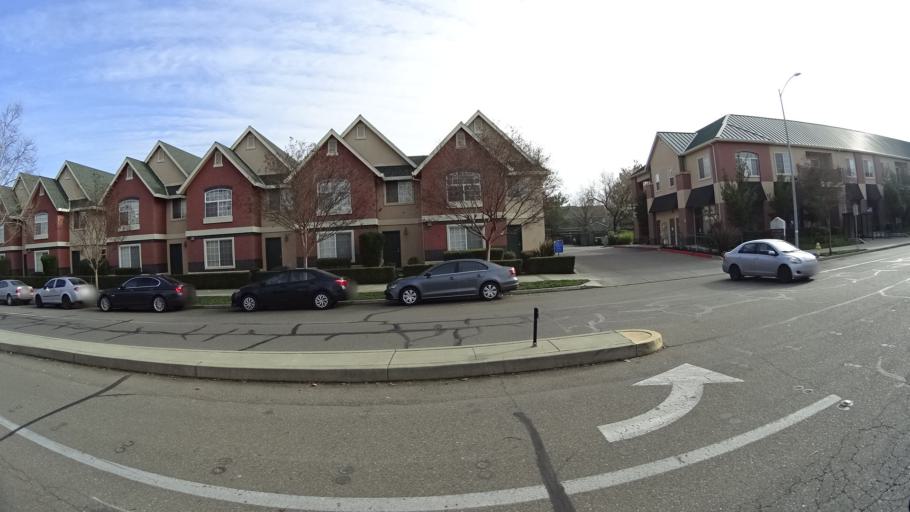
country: US
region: California
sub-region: Yolo County
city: Davis
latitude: 38.5406
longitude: -121.7238
